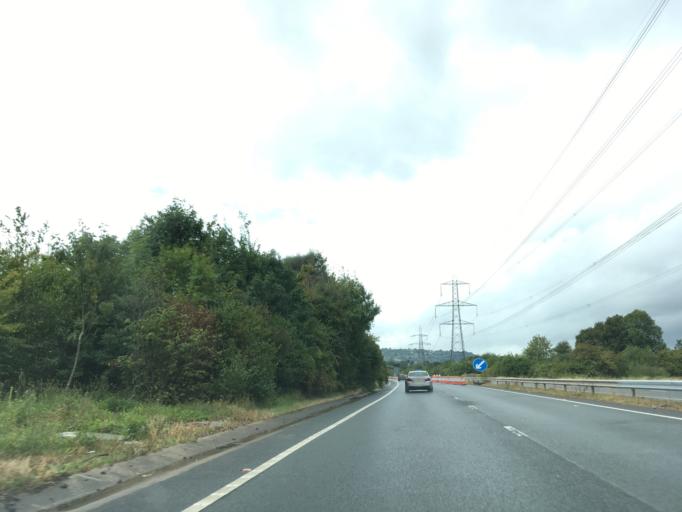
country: GB
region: Wales
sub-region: Monmouthshire
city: Gilwern
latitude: 51.8209
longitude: -3.0586
